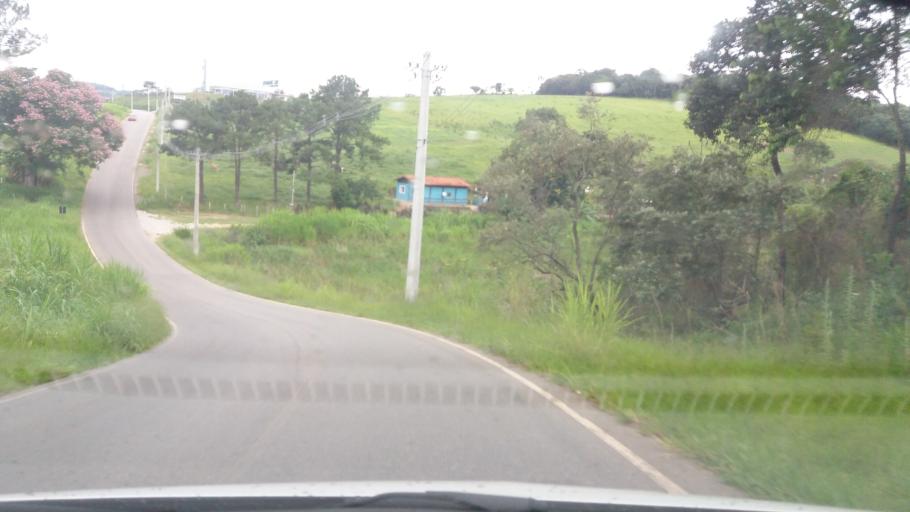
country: BR
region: Sao Paulo
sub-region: Bom Jesus Dos Perdoes
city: Bom Jesus dos Perdoes
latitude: -23.1688
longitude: -46.4438
